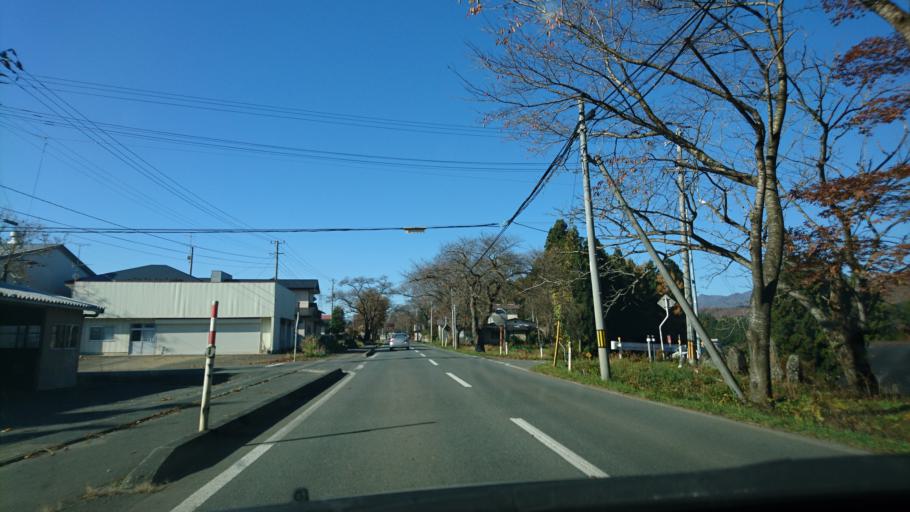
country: JP
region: Iwate
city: Mizusawa
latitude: 39.1272
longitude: 141.0146
